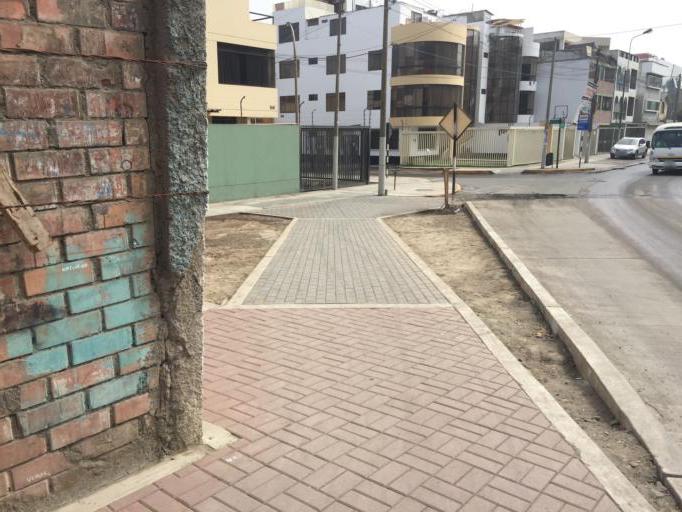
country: PE
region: Lima
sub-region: Lima
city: La Molina
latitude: -12.0713
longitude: -76.9374
